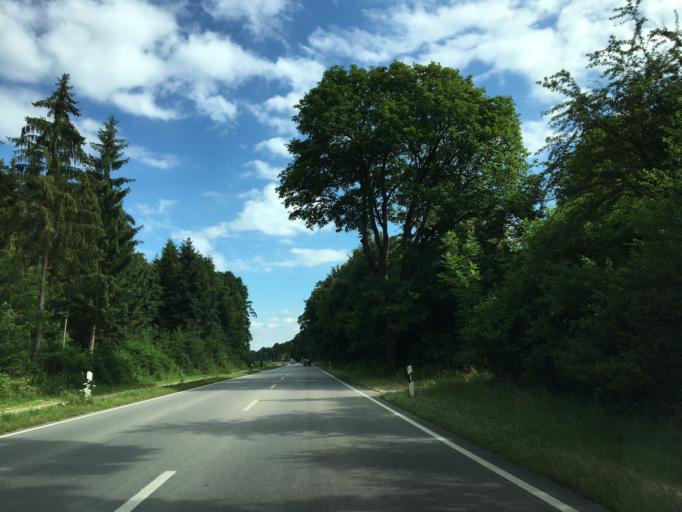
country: DE
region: Bavaria
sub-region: Upper Bavaria
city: Sauerlach
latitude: 47.9608
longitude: 11.6528
